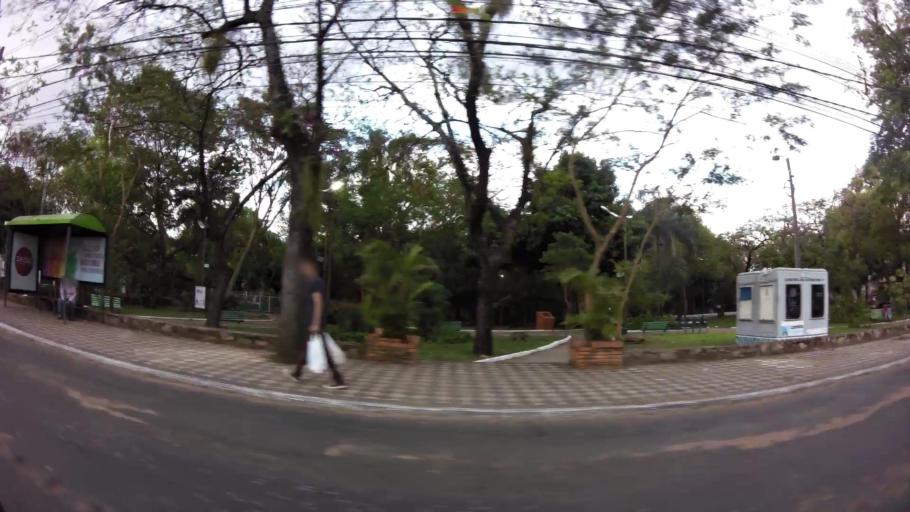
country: PY
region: Asuncion
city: Asuncion
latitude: -25.2899
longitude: -57.5916
